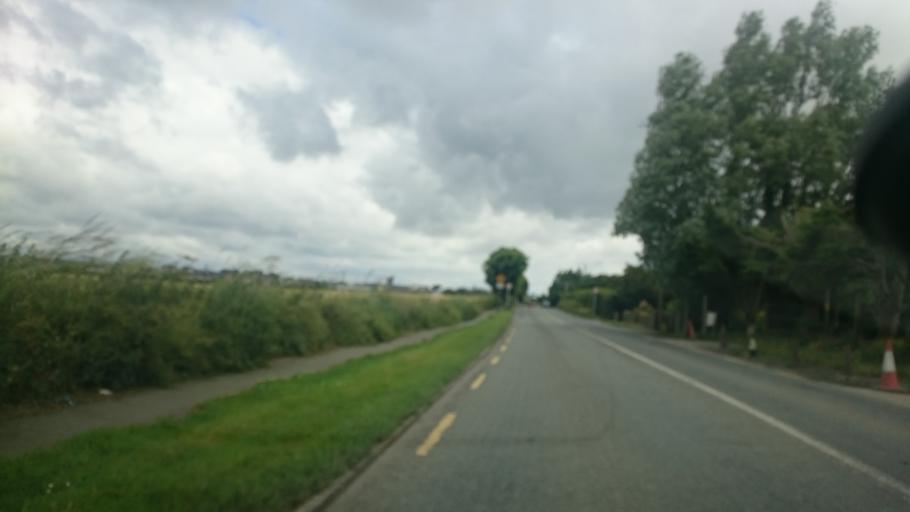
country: IE
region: Leinster
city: Lusk
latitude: 53.5175
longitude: -6.1708
